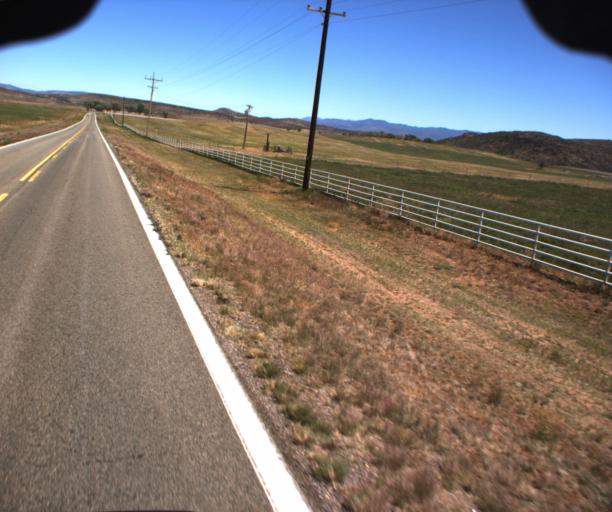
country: US
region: Arizona
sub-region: Yavapai County
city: Congress
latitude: 34.2862
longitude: -112.7228
